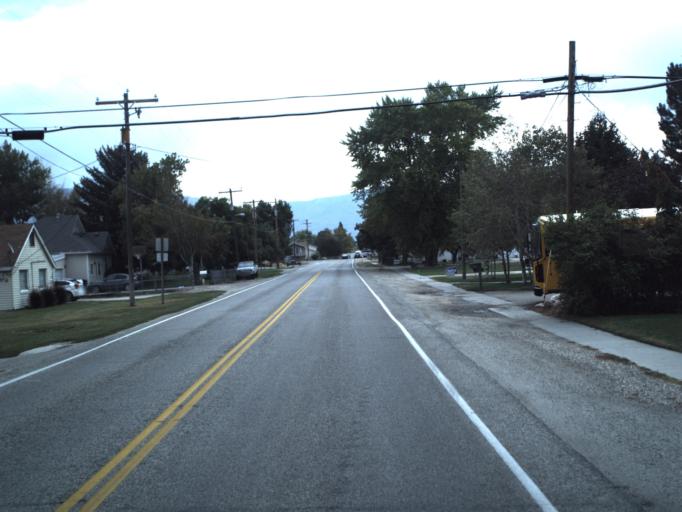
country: US
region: Utah
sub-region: Weber County
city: Plain City
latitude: 41.3047
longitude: -112.0838
